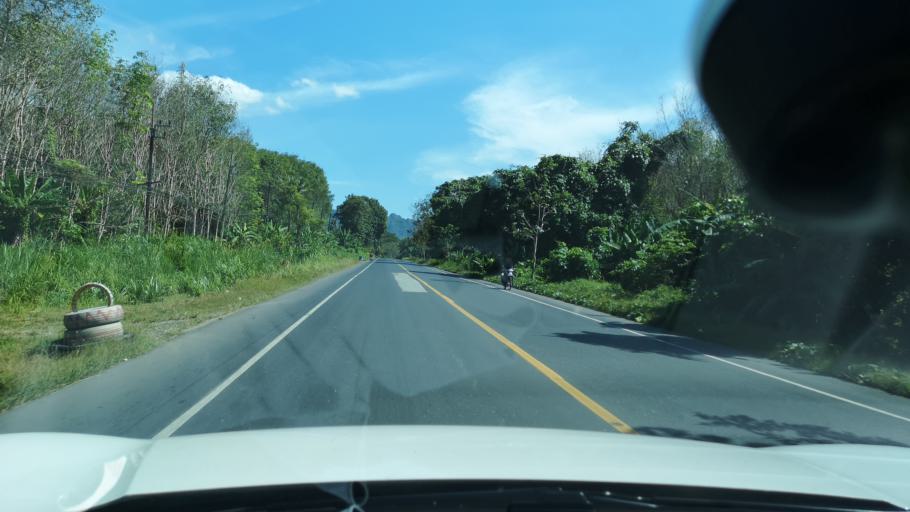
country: TH
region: Phangnga
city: Phang Nga
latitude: 8.5367
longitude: 98.4994
